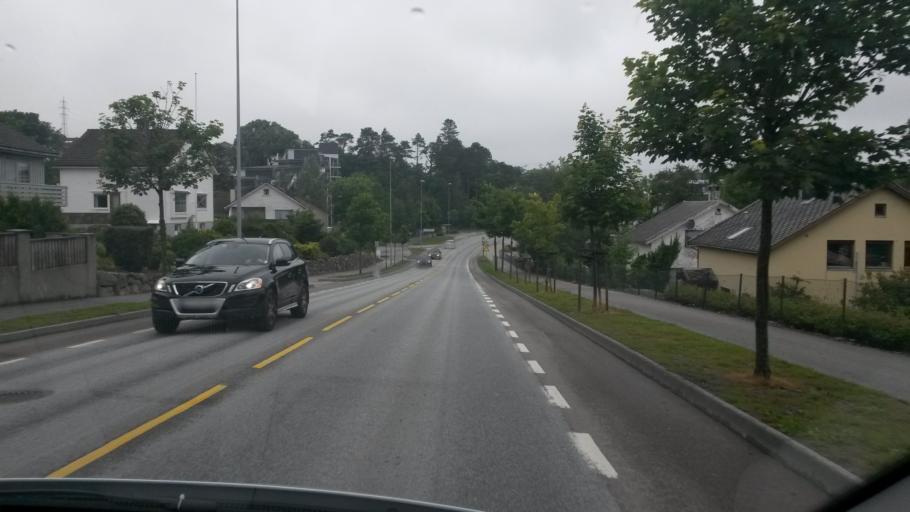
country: NO
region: Rogaland
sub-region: Sandnes
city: Sandnes
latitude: 58.8322
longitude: 5.7185
